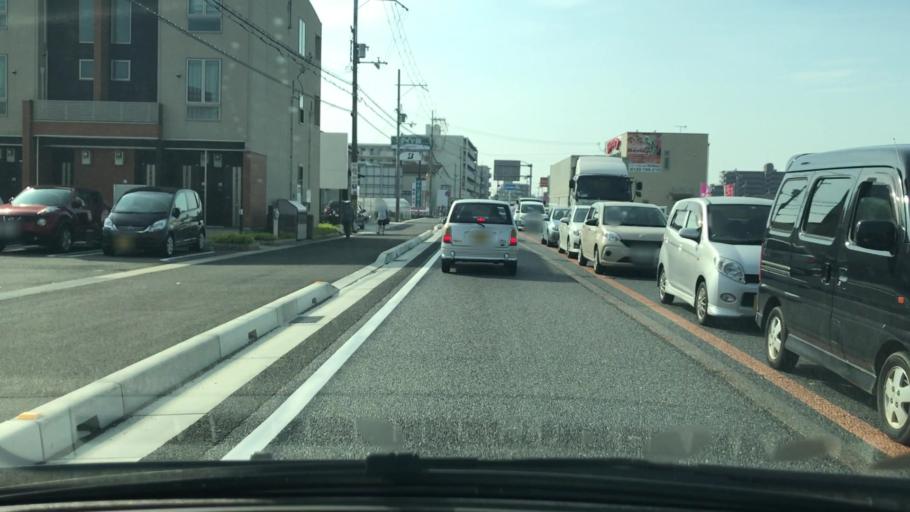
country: JP
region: Hyogo
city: Kakogawacho-honmachi
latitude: 34.7184
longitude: 134.8954
